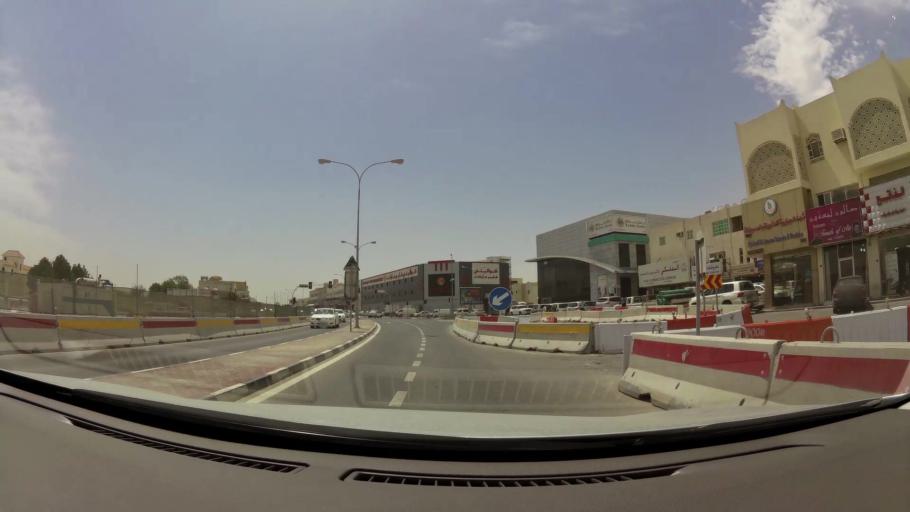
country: QA
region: Baladiyat ar Rayyan
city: Ar Rayyan
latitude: 25.3001
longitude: 51.4201
